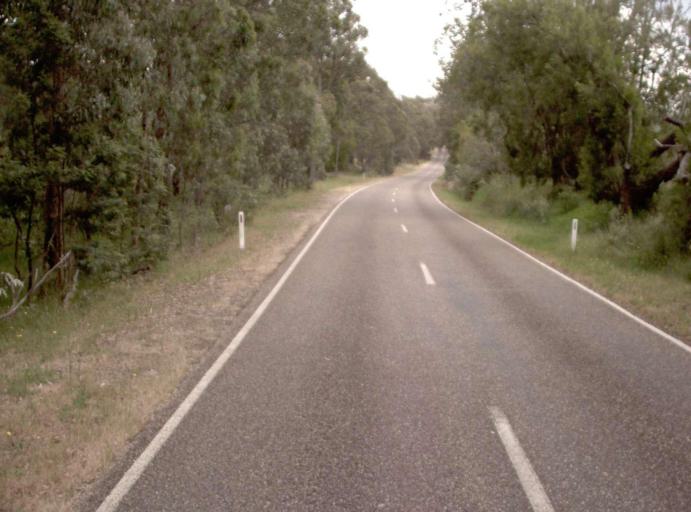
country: AU
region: Victoria
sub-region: East Gippsland
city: Bairnsdale
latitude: -37.7824
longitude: 147.3240
